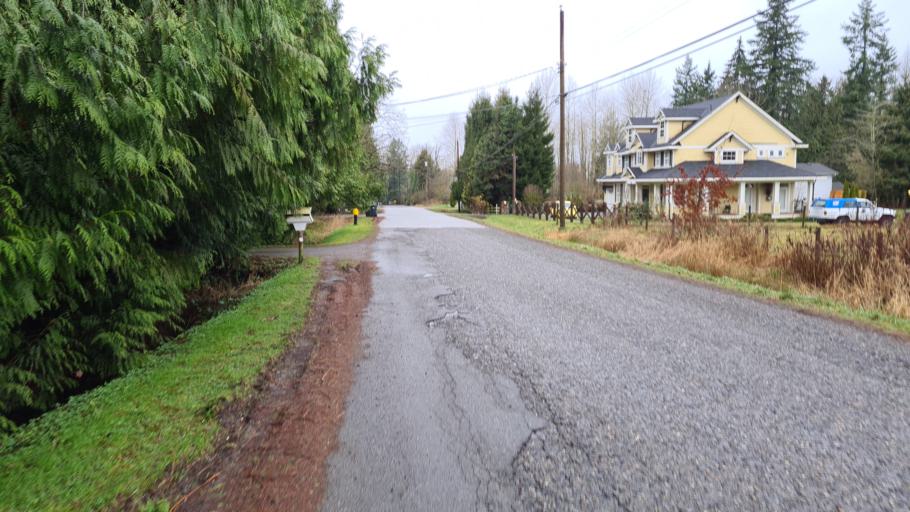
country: CA
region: British Columbia
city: Walnut Grove
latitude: 49.1384
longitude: -122.6565
